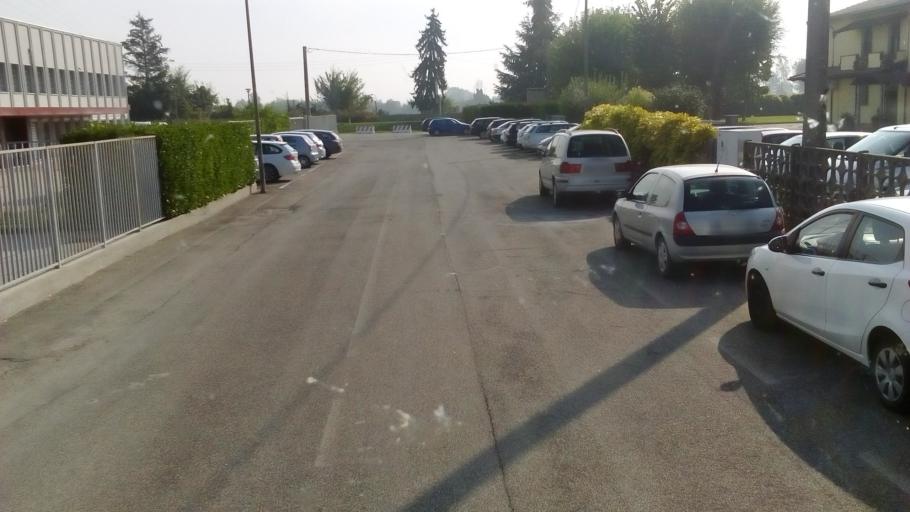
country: IT
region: Lombardy
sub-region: Provincia di Mantova
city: Ostiglia
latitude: 45.0882
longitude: 11.1378
